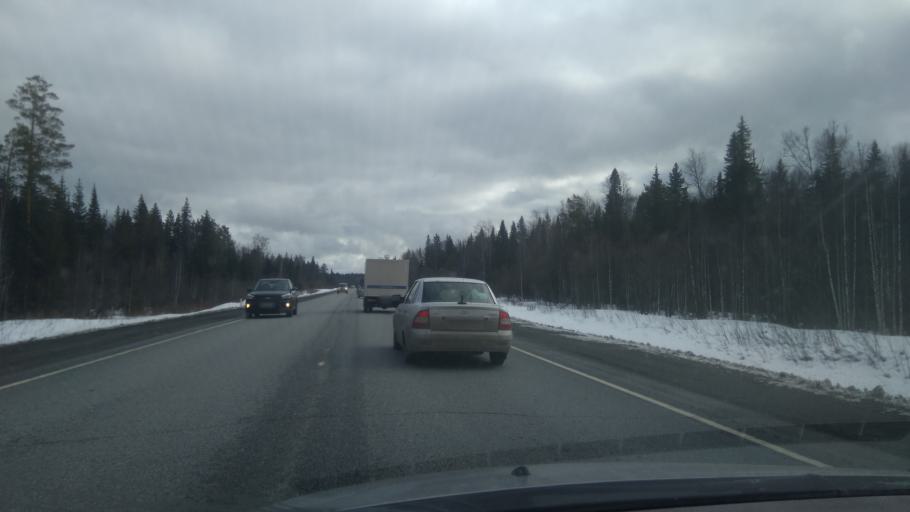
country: RU
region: Sverdlovsk
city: Atig
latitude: 56.8124
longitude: 59.3606
